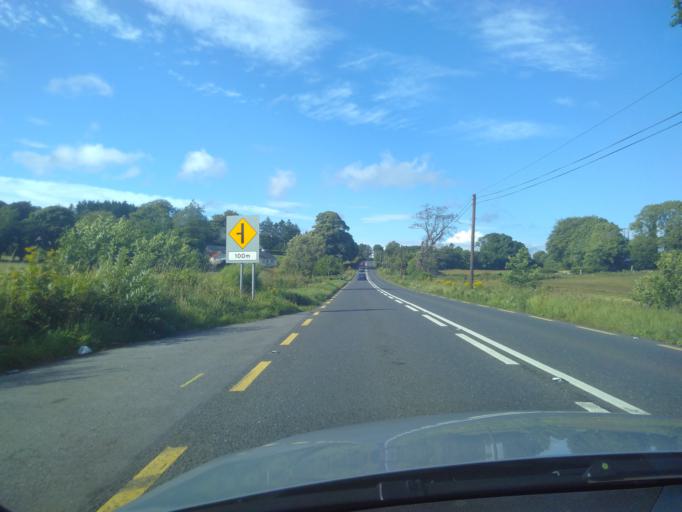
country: IE
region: Ulster
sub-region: County Donegal
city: Ballybofey
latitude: 54.8171
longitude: -7.7576
